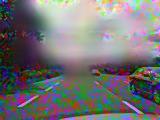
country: IE
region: Ulster
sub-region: County Donegal
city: Letterkenny
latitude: 54.8799
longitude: -7.7406
